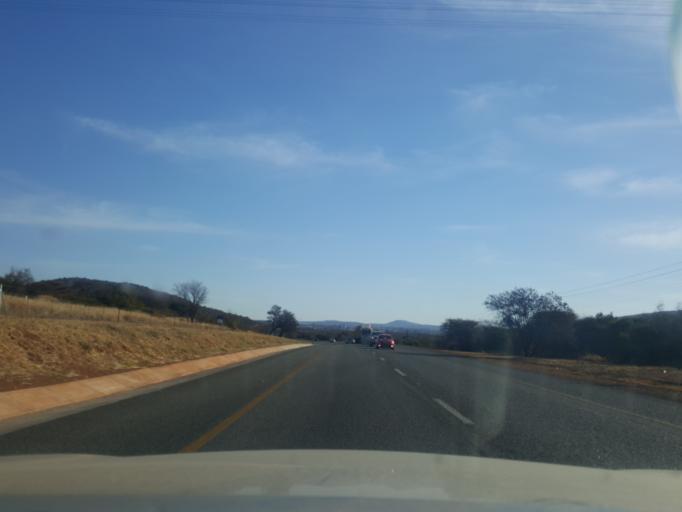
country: ZA
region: North-West
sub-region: Ngaka Modiri Molema District Municipality
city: Zeerust
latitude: -25.5375
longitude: 26.1275
